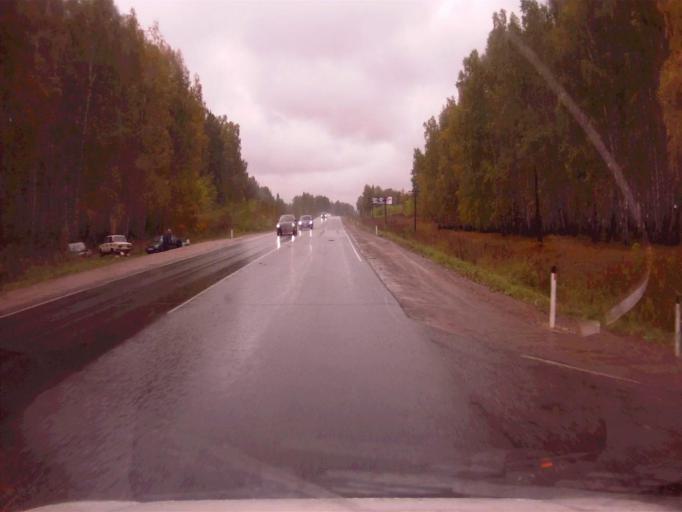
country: RU
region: Chelyabinsk
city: Argayash
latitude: 55.4675
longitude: 60.9081
